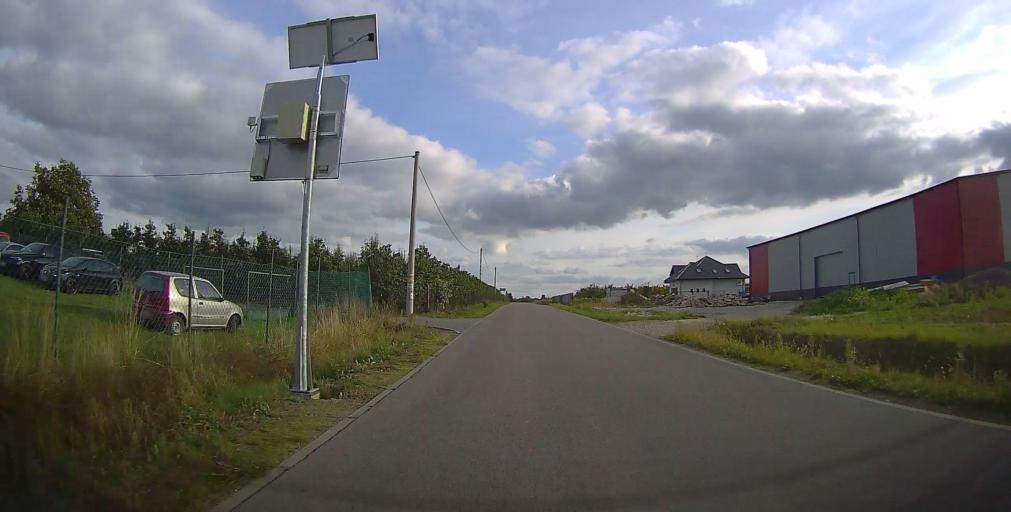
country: PL
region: Masovian Voivodeship
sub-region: Powiat grojecki
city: Jasieniec
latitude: 51.7534
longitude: 20.9621
